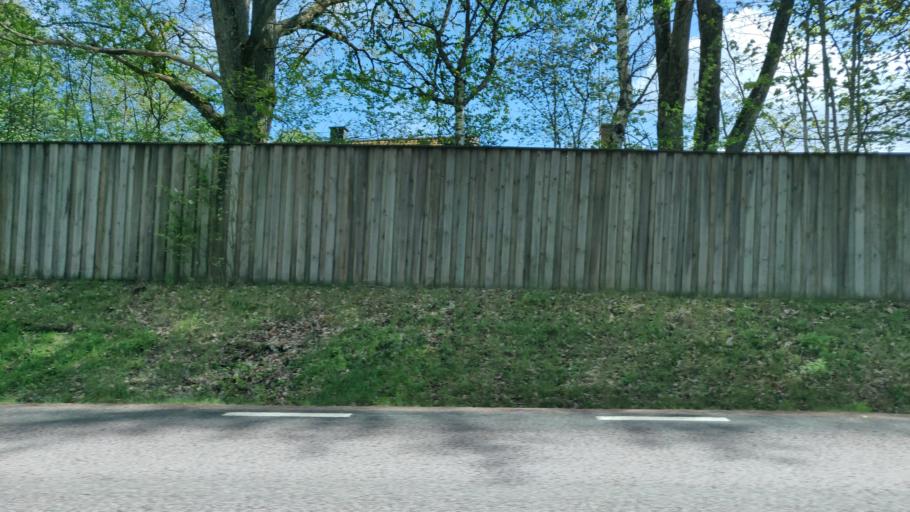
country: SE
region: Vaermland
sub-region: Karlstads Kommun
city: Skattkarr
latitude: 59.5007
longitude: 13.6145
